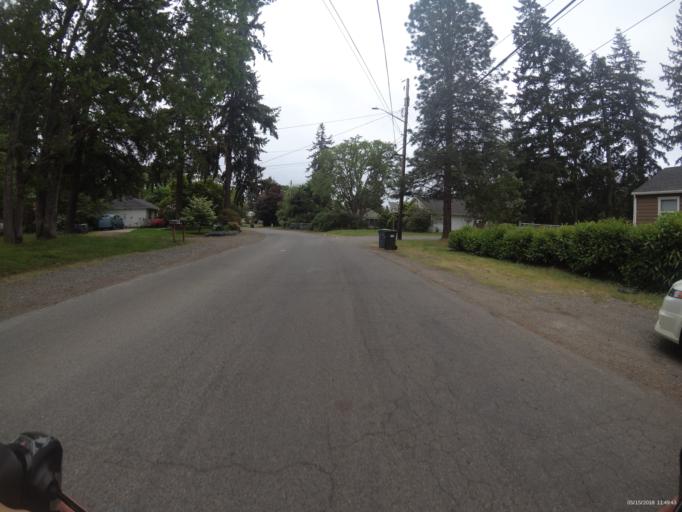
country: US
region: Washington
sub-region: Pierce County
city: Lakewood
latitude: 47.1762
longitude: -122.5237
